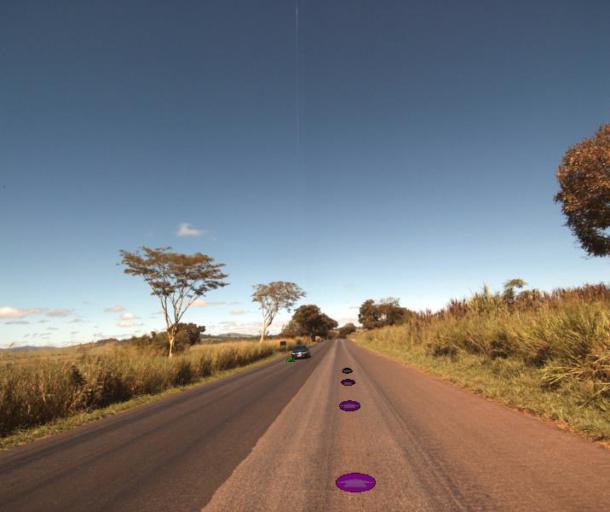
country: BR
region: Goias
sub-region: Itapaci
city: Itapaci
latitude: -15.1227
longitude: -49.5031
